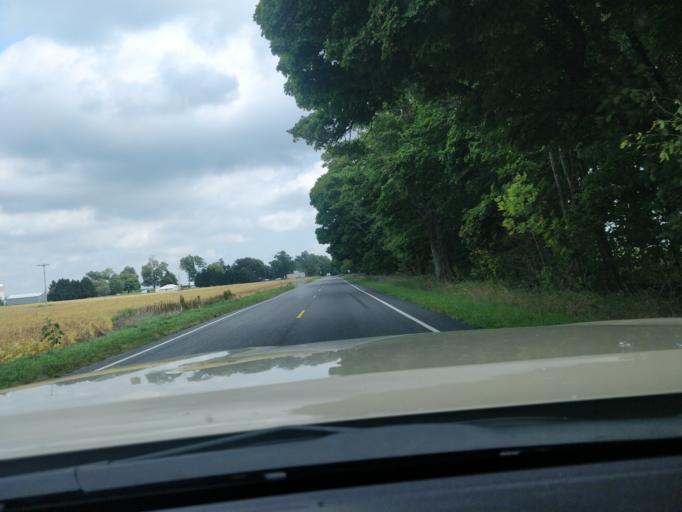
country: US
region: Michigan
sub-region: Kent County
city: Lowell
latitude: 42.8860
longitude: -85.2975
